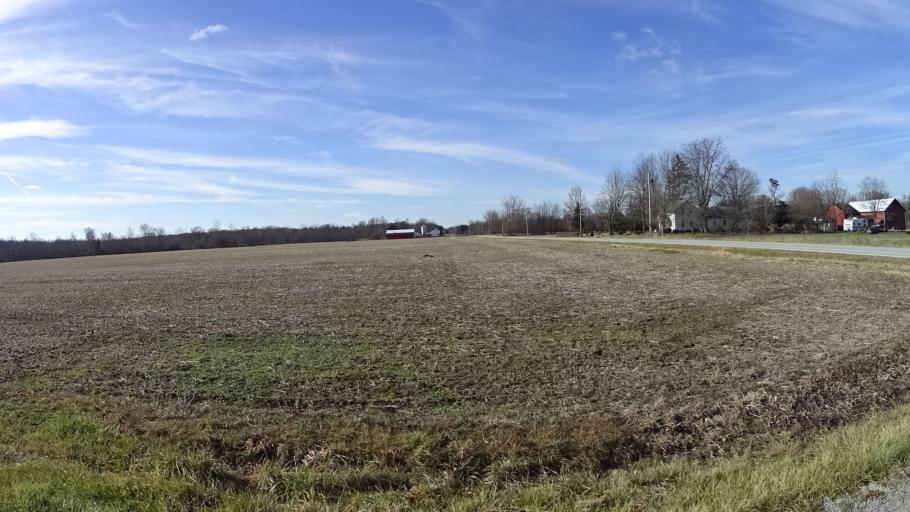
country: US
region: Ohio
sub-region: Lorain County
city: Wellington
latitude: 41.1010
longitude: -82.2395
